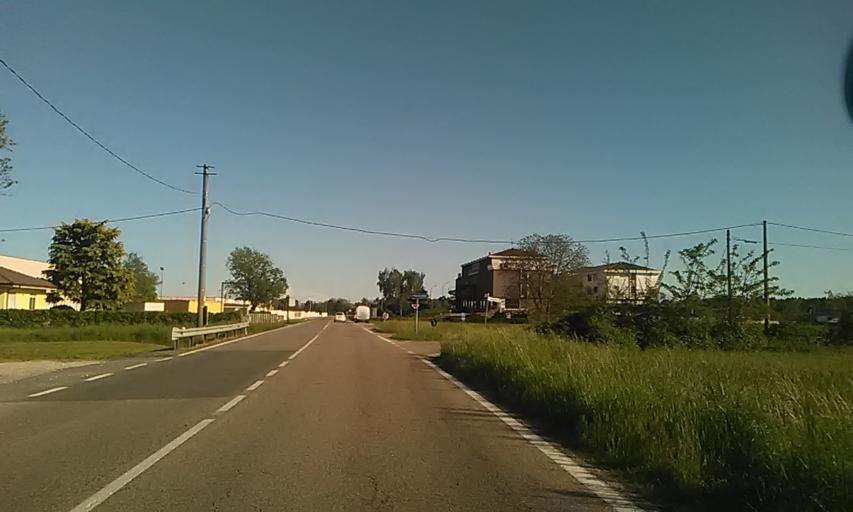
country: IT
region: Piedmont
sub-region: Provincia di Novara
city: Cavaglietto
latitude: 45.6096
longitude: 8.5220
